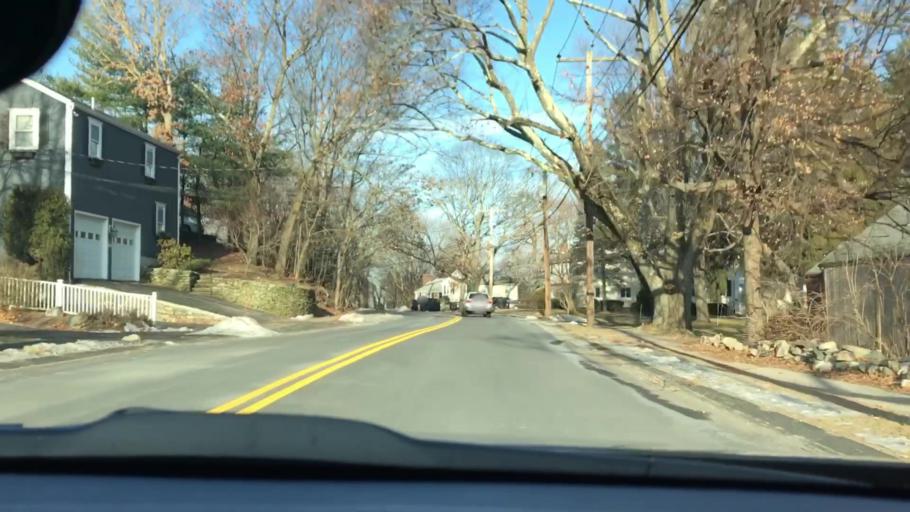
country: US
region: Massachusetts
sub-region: Norfolk County
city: Needham
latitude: 42.2959
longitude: -71.2235
